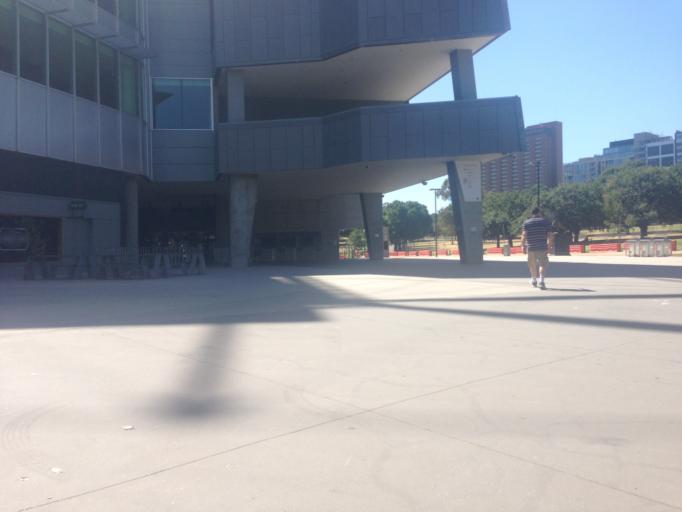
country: AU
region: Victoria
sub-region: Melbourne
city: East Melbourne
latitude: -37.8194
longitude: 144.9850
